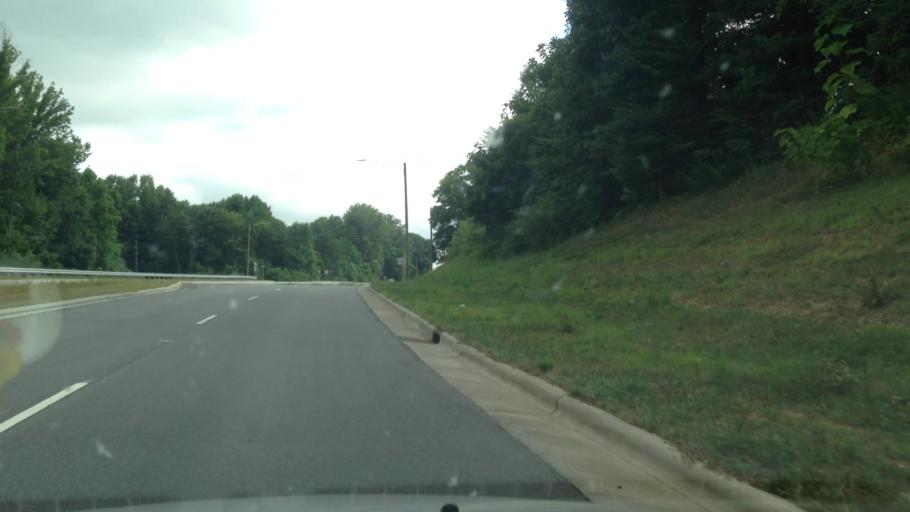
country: US
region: North Carolina
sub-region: Rockingham County
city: Reidsville
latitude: 36.3717
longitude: -79.6770
